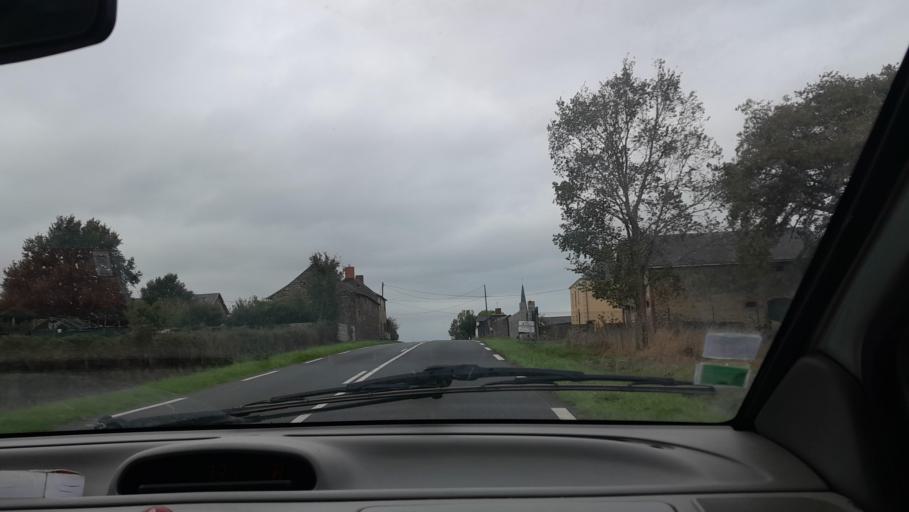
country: FR
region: Pays de la Loire
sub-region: Departement de la Loire-Atlantique
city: Saint-Mars-la-Jaille
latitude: 47.5812
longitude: -1.1914
